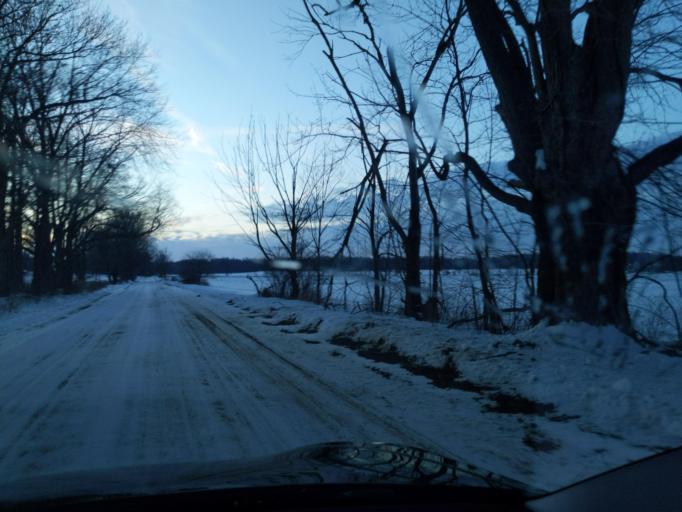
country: US
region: Michigan
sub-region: Ingham County
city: Mason
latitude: 42.5704
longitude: -84.3522
